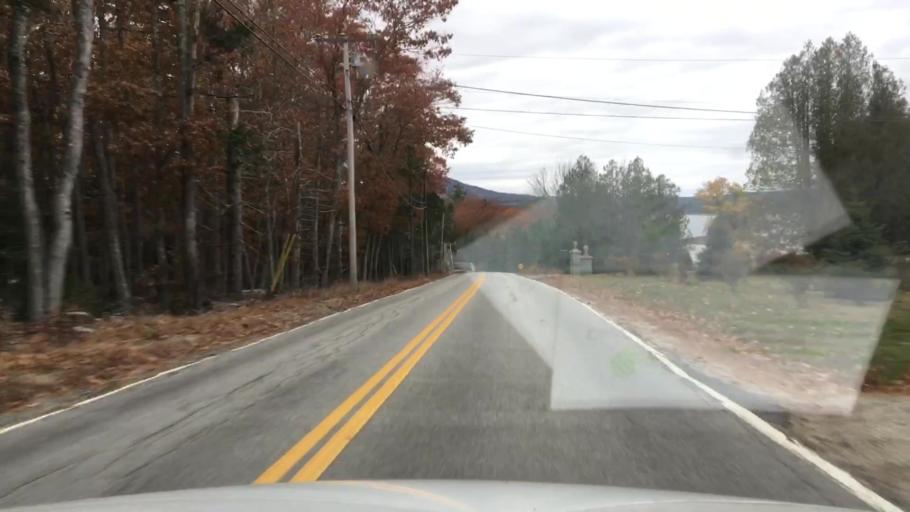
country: US
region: Maine
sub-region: Hancock County
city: Sedgwick
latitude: 44.3716
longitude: -68.5582
